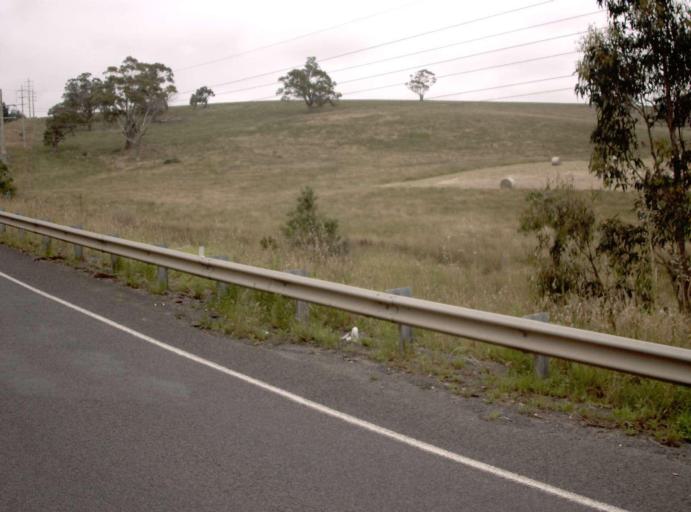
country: AU
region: Victoria
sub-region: Latrobe
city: Traralgon
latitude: -38.2488
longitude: 146.5284
